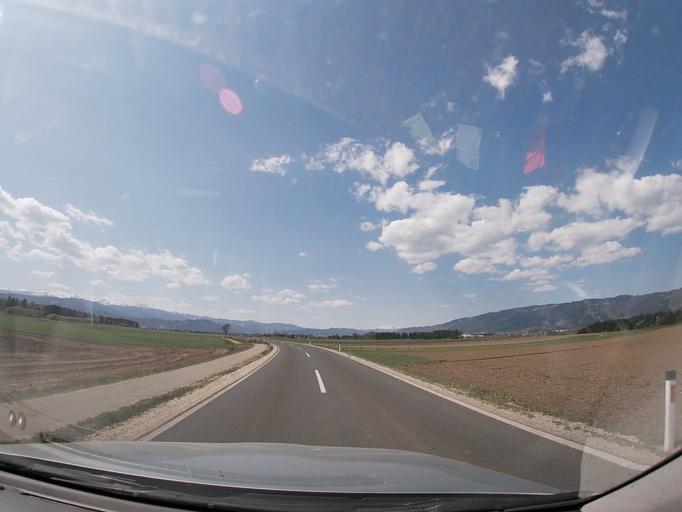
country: AT
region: Styria
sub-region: Politischer Bezirk Murtal
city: Grosslobming
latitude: 47.1816
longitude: 14.7903
